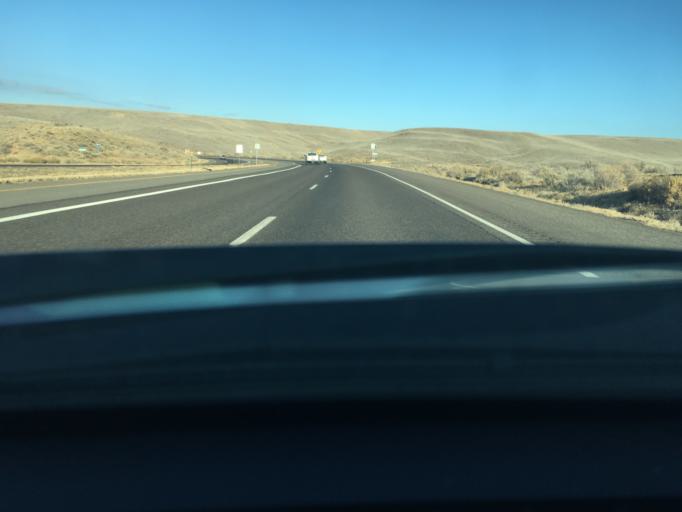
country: US
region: Colorado
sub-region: Delta County
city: Delta
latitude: 38.8091
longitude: -108.2787
